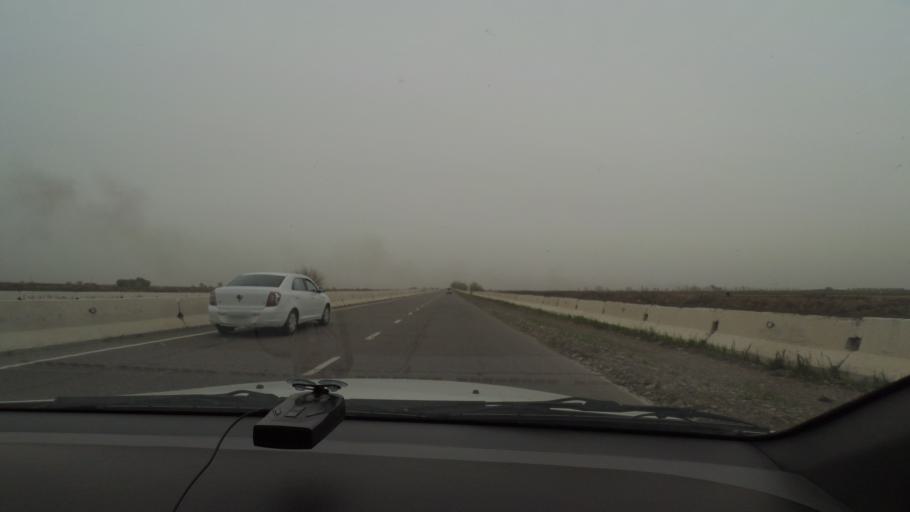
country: UZ
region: Jizzax
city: Gagarin
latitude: 40.5133
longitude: 68.3243
